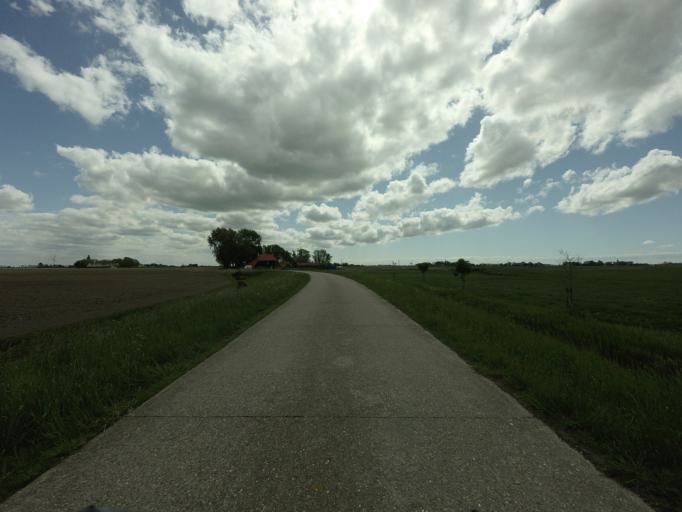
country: NL
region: Friesland
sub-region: Gemeente Littenseradiel
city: Wommels
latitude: 53.1181
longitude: 5.5508
